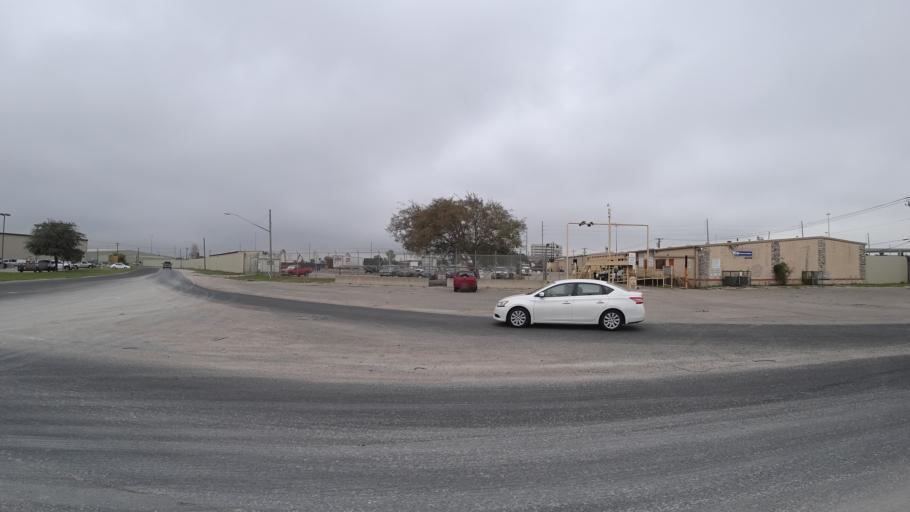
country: US
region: Texas
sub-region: Travis County
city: Austin
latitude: 30.2148
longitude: -97.7572
